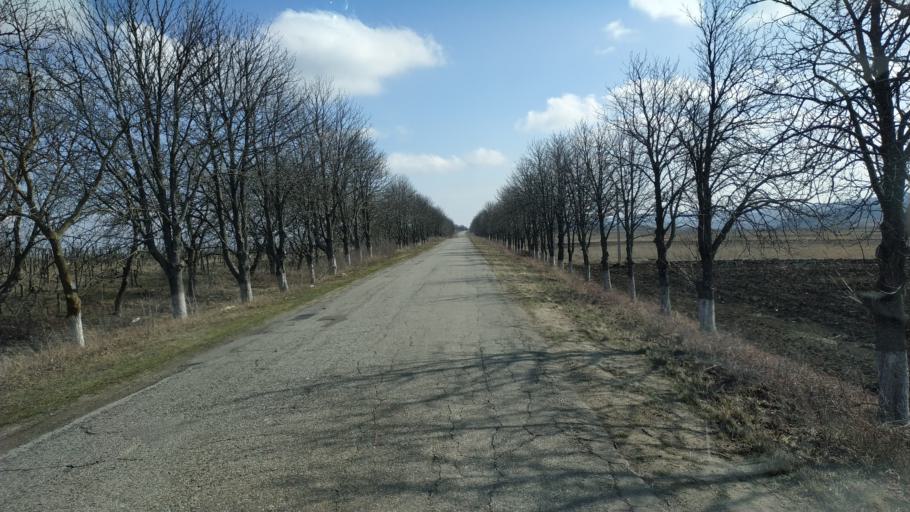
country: MD
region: Hincesti
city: Hincesti
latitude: 46.8548
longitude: 28.6407
